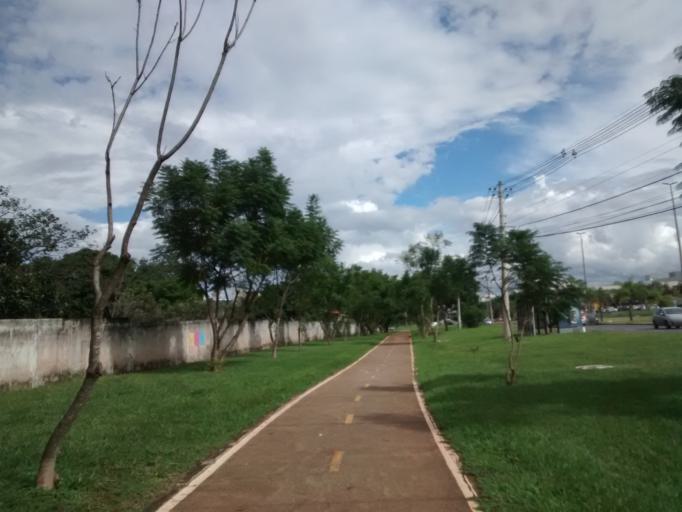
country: BR
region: Federal District
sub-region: Brasilia
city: Brasilia
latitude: -15.7921
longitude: -47.9160
